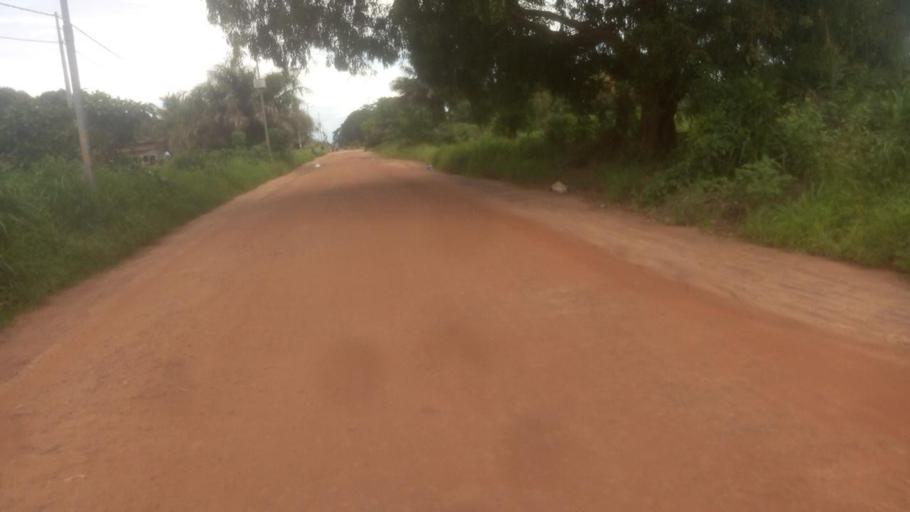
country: SL
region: Northern Province
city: Masoyila
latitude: 8.6020
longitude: -13.1933
